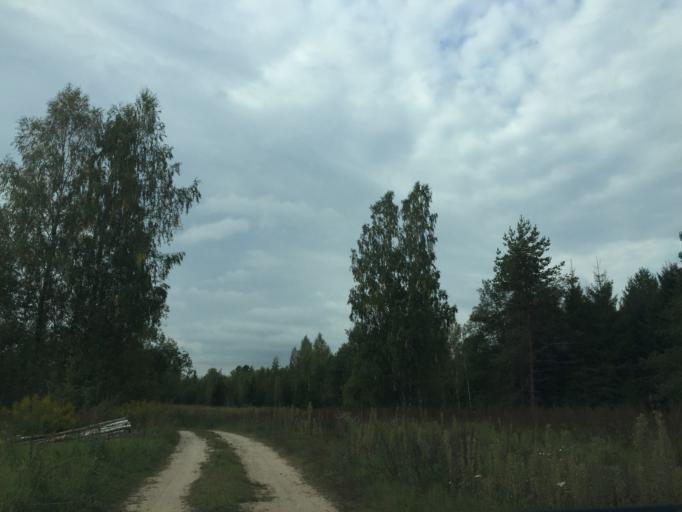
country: LV
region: Baldone
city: Baldone
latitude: 56.7658
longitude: 24.4617
